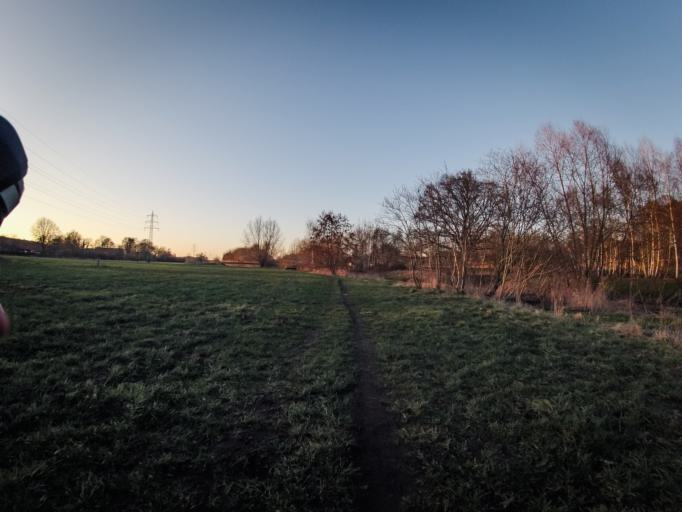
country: DE
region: Lower Saxony
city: Wallenhorst
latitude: 52.3139
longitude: 7.9765
